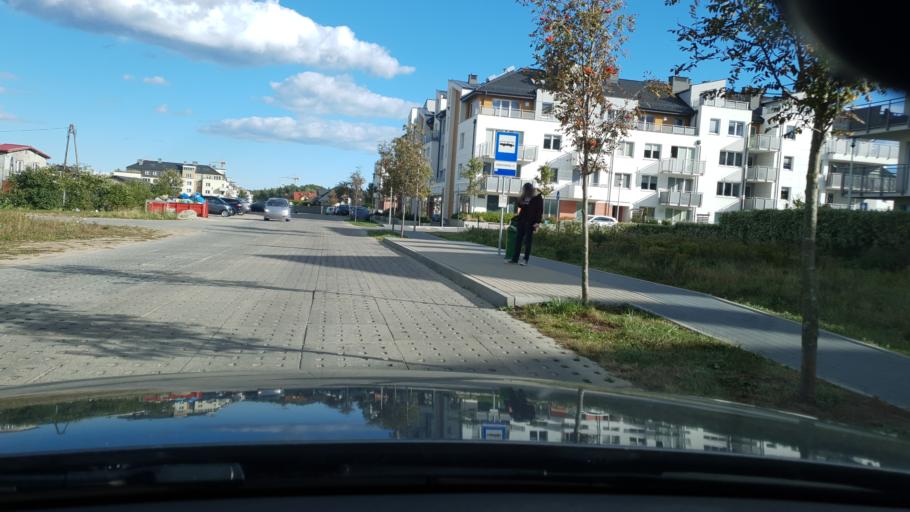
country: PL
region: Pomeranian Voivodeship
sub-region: Powiat kartuski
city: Chwaszczyno
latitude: 54.4930
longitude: 18.4339
